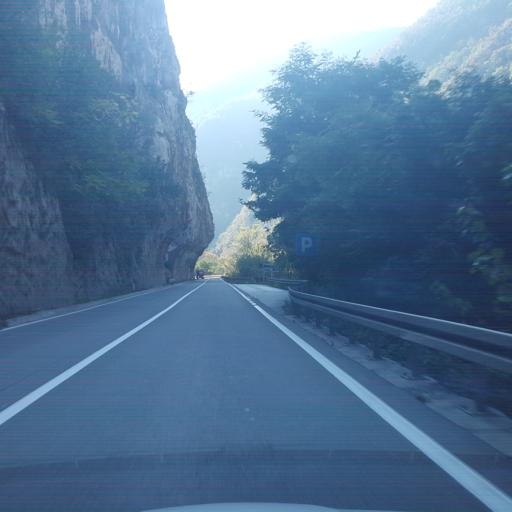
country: RS
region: Central Serbia
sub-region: Nisavski Okrug
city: Svrljig
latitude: 43.3251
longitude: 22.1642
